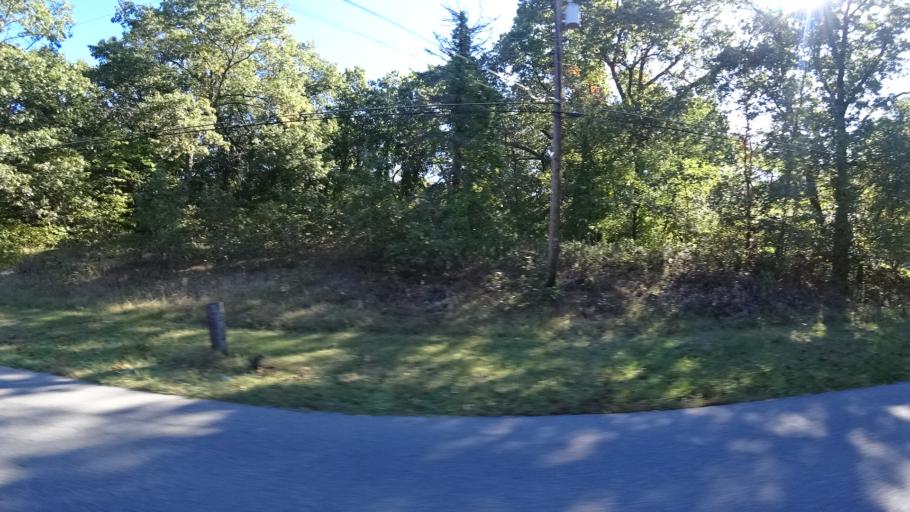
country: US
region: Indiana
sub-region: LaPorte County
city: Michigan City
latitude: 41.6920
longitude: -86.9324
